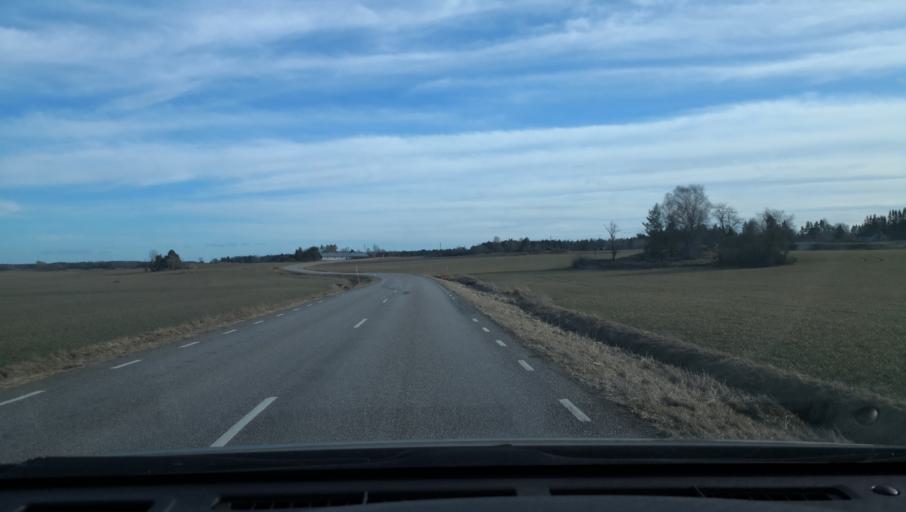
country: SE
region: Uppsala
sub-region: Enkopings Kommun
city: Enkoping
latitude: 59.6120
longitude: 17.1093
